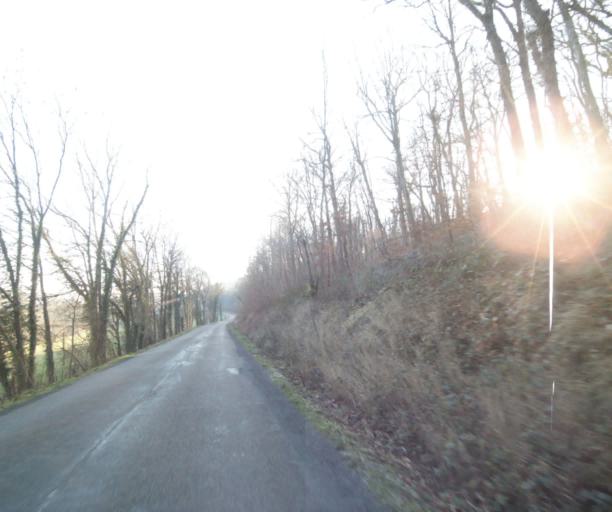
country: FR
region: Champagne-Ardenne
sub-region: Departement de la Haute-Marne
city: Bienville
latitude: 48.5681
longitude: 5.0792
